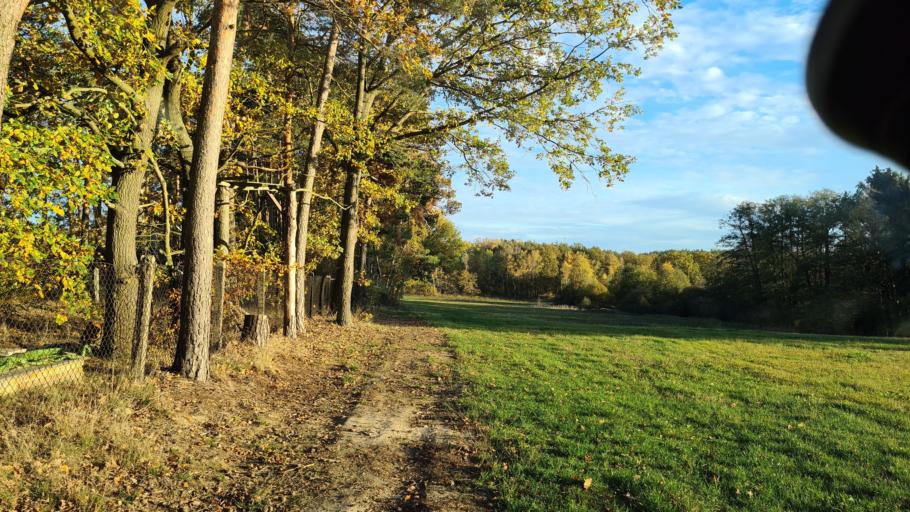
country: DE
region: Saxony
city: Dahlen
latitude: 51.4006
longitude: 12.9964
